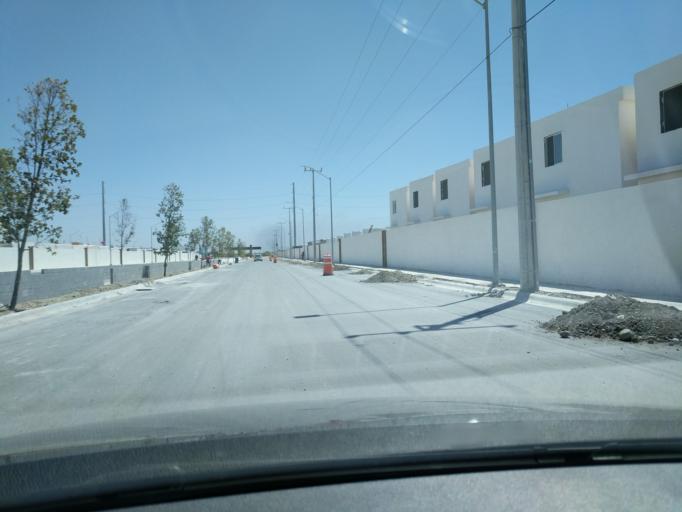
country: MX
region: Nuevo Leon
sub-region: Apodaca
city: Artemio Trevino
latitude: 25.8424
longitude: -100.1397
